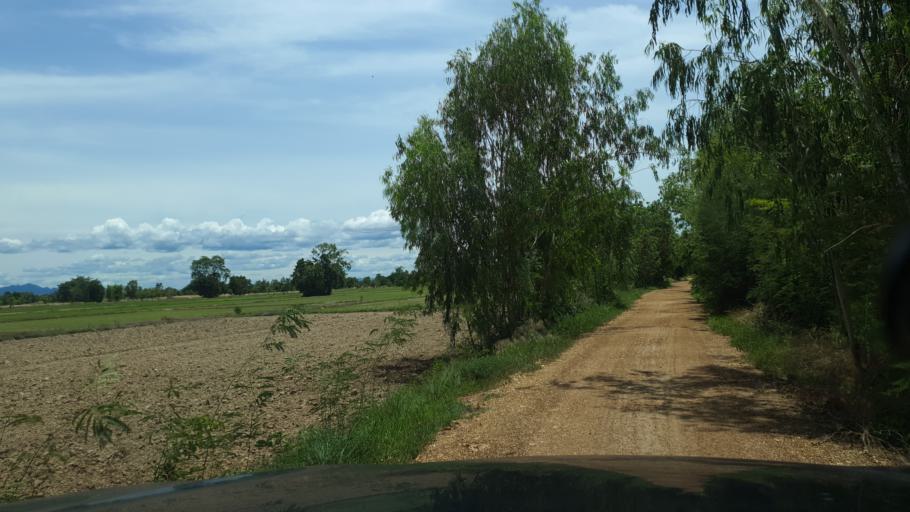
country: TH
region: Sukhothai
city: Ban Na
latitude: 17.1302
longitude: 99.6707
